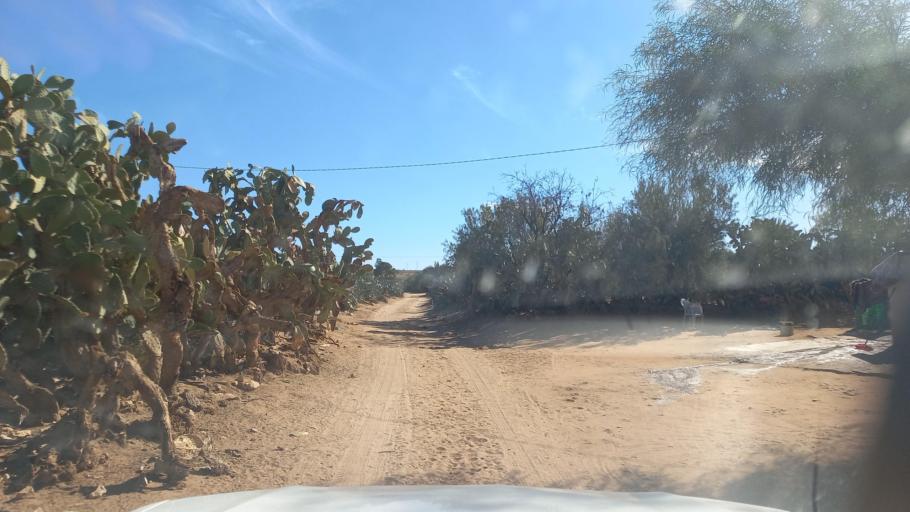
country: TN
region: Al Qasrayn
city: Kasserine
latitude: 35.2103
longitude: 8.9716
